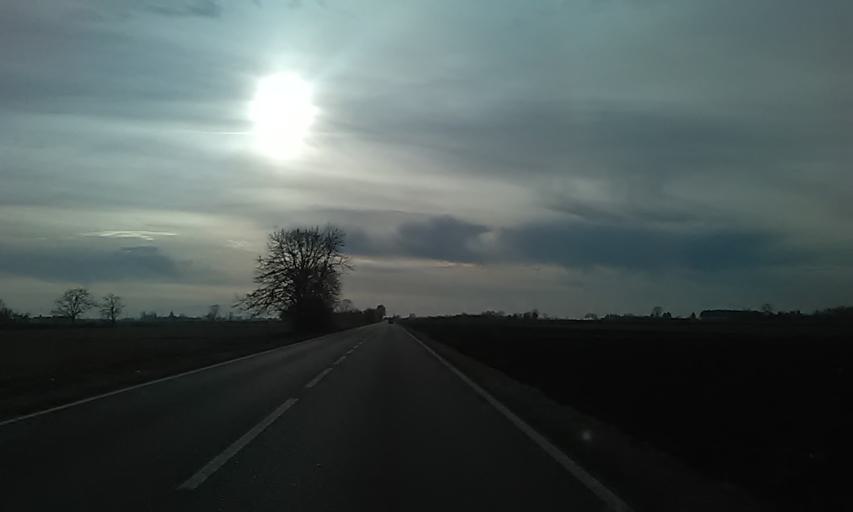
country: IT
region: Piedmont
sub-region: Provincia di Torino
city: Villareggia
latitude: 45.2910
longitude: 7.9985
